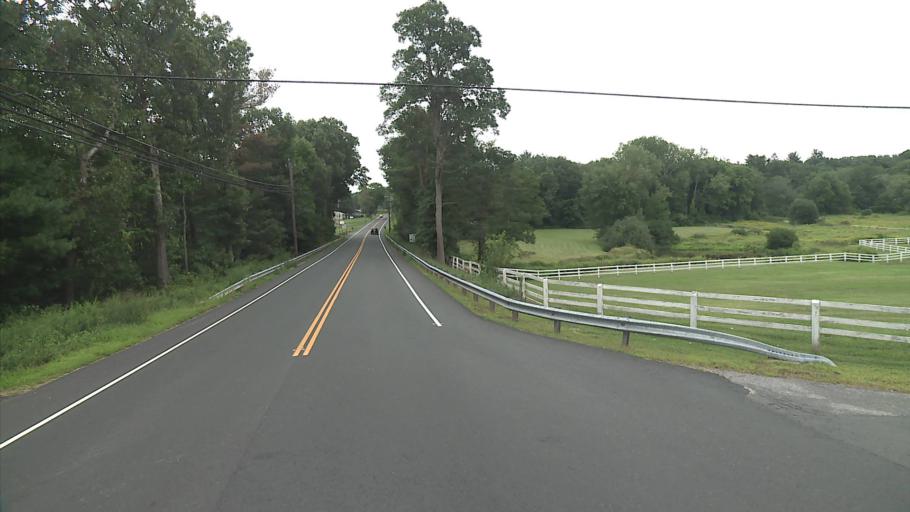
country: US
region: Connecticut
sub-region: Tolland County
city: Rockville
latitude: 41.8691
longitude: -72.4179
